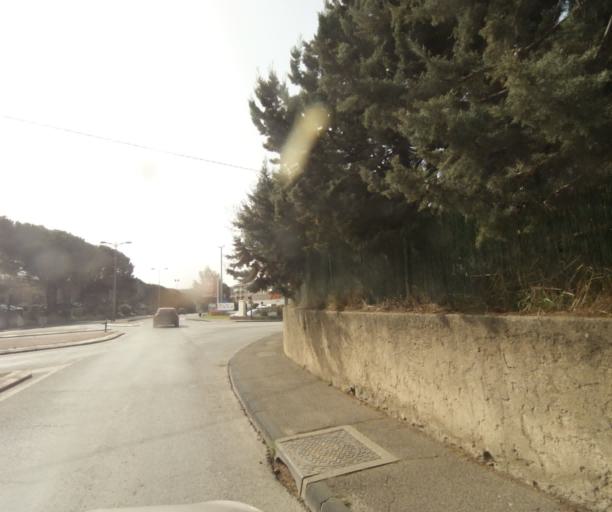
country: FR
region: Provence-Alpes-Cote d'Azur
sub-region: Departement des Bouches-du-Rhone
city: Gardanne
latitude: 43.4544
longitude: 5.4767
